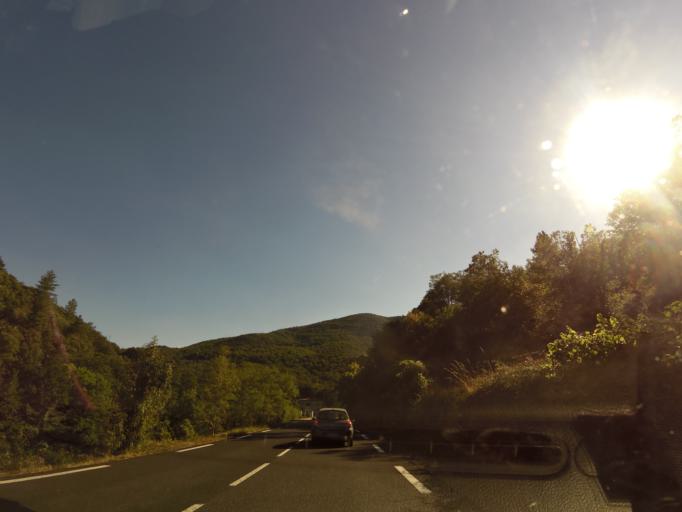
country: FR
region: Languedoc-Roussillon
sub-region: Departement du Gard
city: Valleraugue
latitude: 44.0417
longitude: 3.6740
